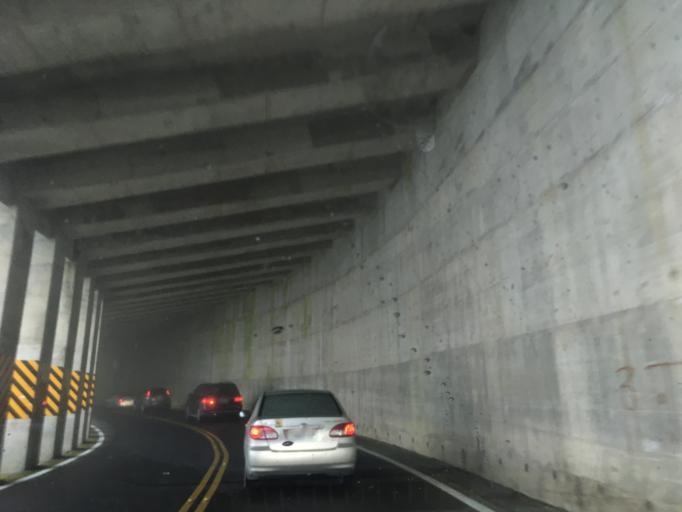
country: TW
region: Taiwan
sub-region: Hualien
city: Hualian
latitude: 24.1880
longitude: 121.4127
